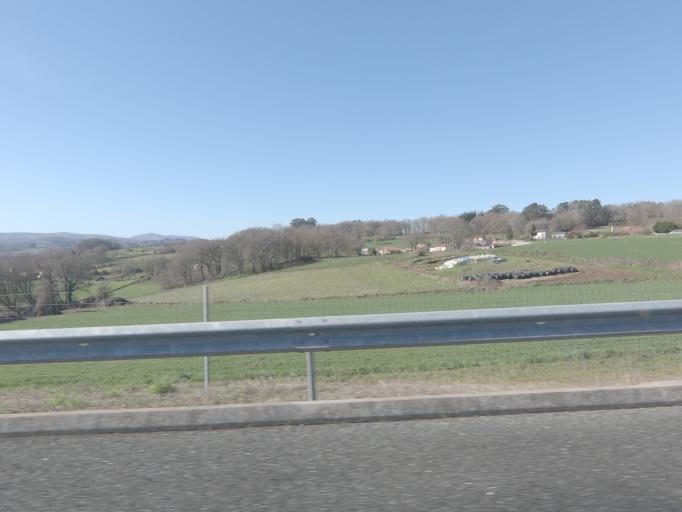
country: ES
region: Galicia
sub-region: Provincia de Pontevedra
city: Lalin
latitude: 42.6469
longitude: -8.1332
